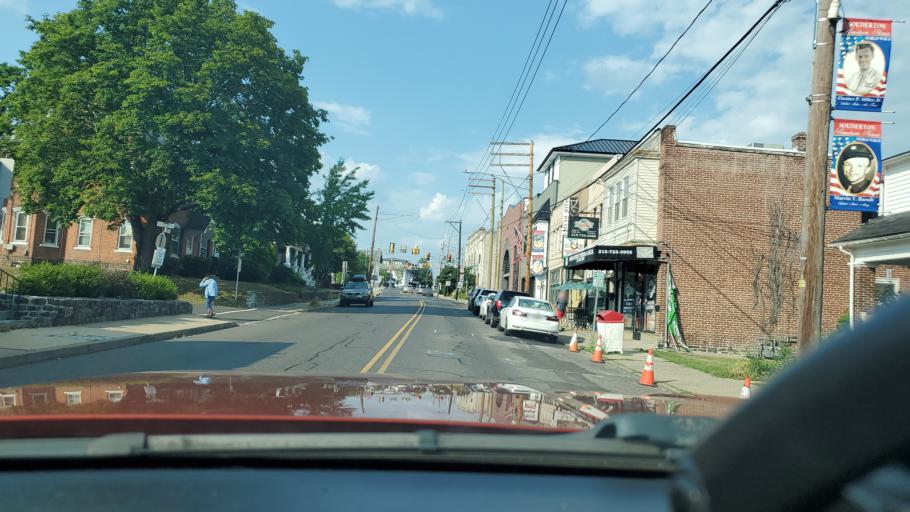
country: US
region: Pennsylvania
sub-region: Montgomery County
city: Souderton
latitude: 40.3082
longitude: -75.3224
